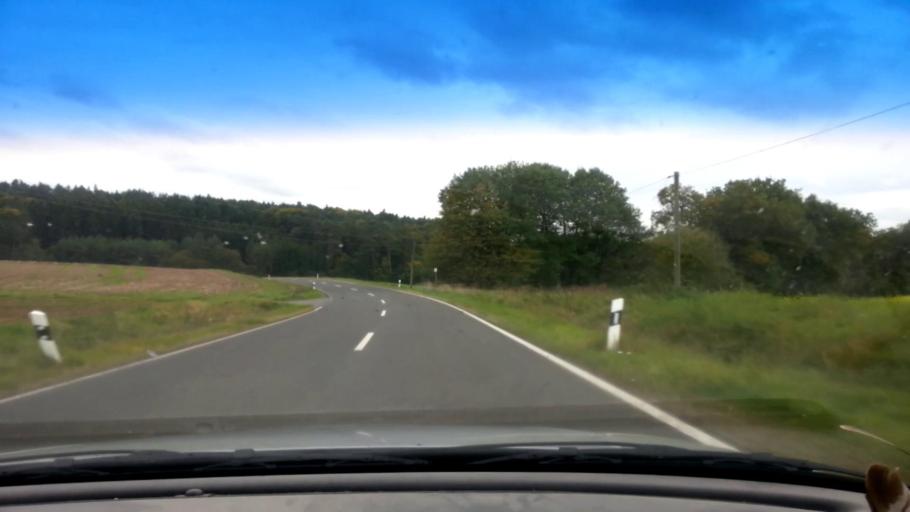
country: DE
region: Bavaria
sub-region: Regierungsbezirk Unterfranken
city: Kirchlauter
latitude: 50.0287
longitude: 10.7396
